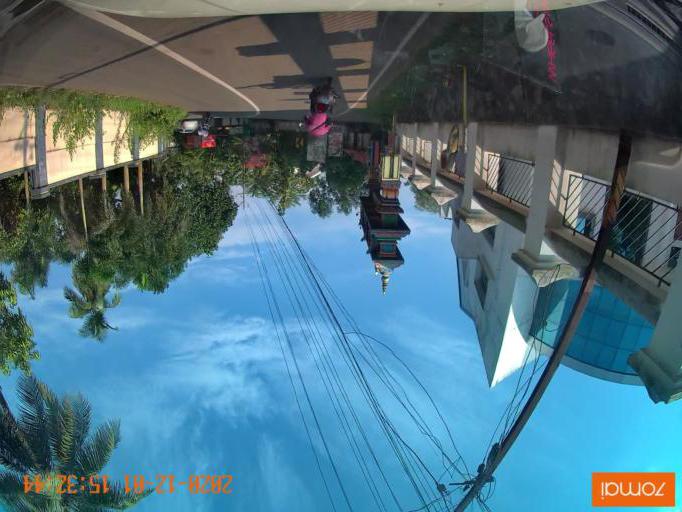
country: IN
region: Kerala
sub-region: Ernakulam
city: Muvattupuzha
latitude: 9.9745
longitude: 76.5741
